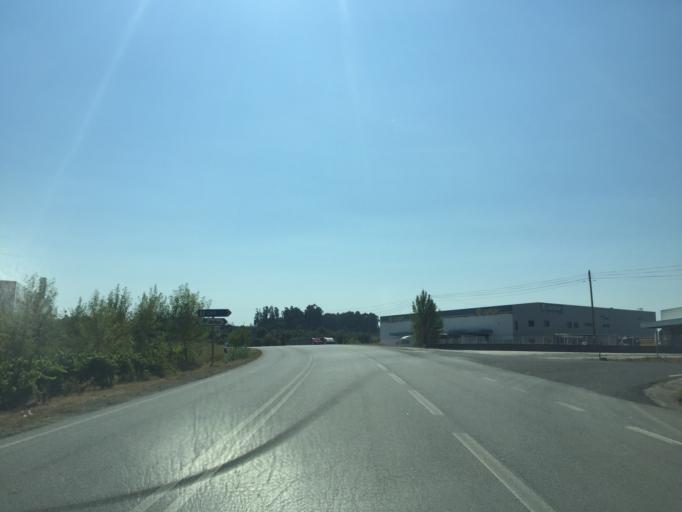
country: PT
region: Aveiro
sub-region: Mealhada
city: Mealhada
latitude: 40.3703
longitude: -8.4872
